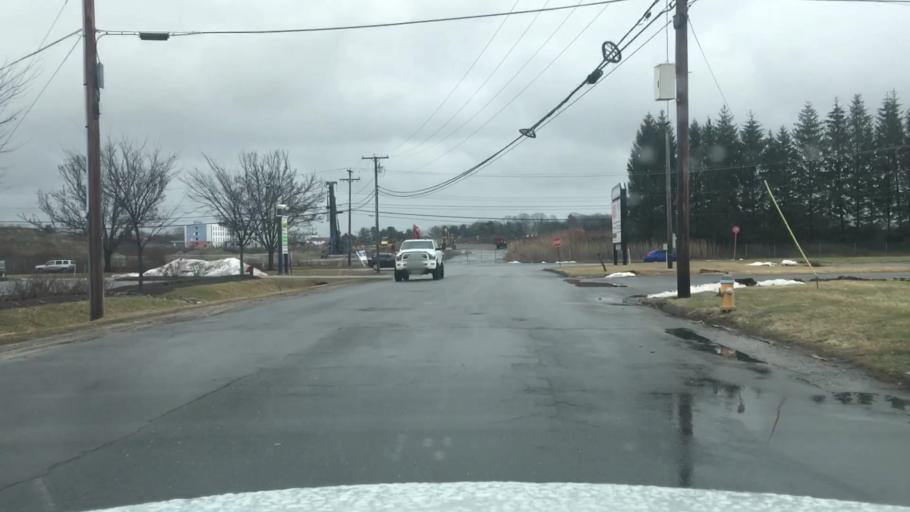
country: US
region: Maine
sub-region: Cumberland County
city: Westbrook
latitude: 43.6755
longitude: -70.3359
